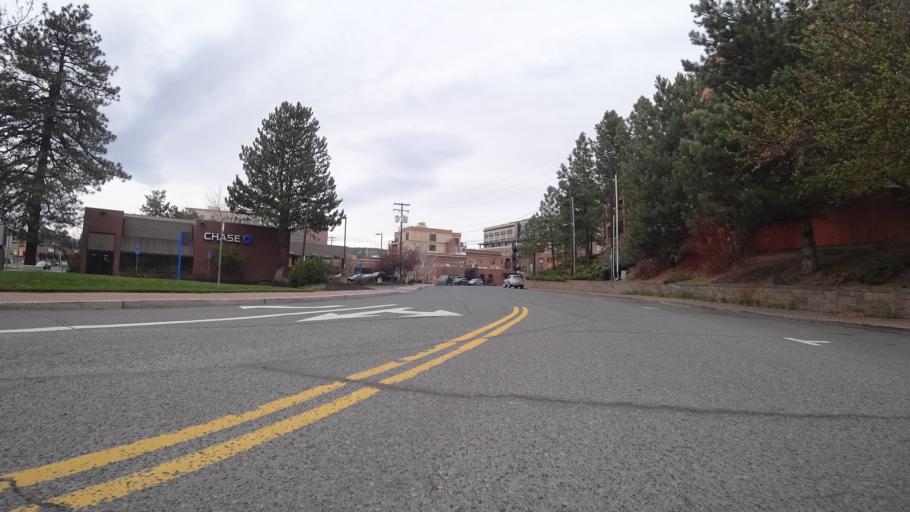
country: US
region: Oregon
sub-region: Deschutes County
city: Bend
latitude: 44.0567
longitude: -121.3119
